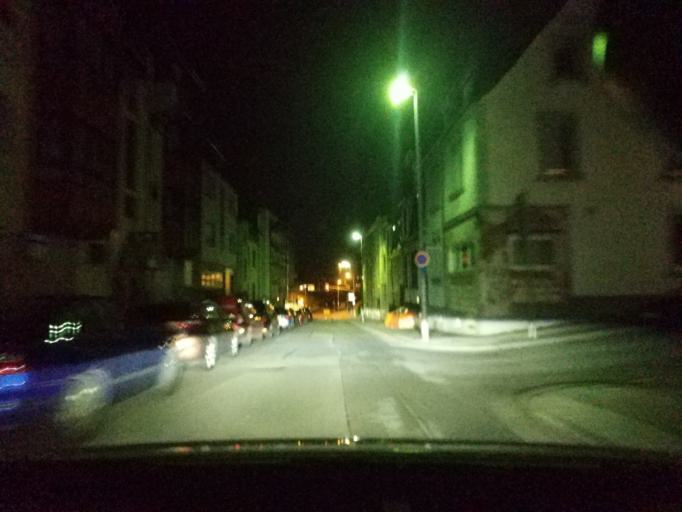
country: DE
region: Rheinland-Pfalz
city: Kaiserslautern
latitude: 49.4326
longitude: 7.7608
